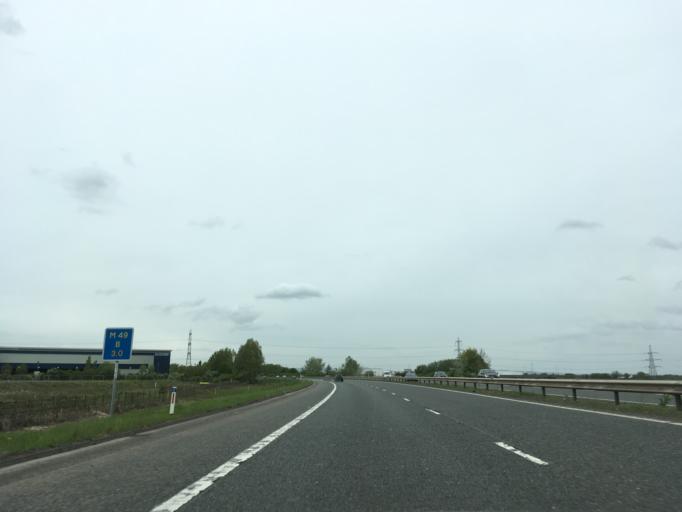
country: GB
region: England
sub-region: South Gloucestershire
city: Severn Beach
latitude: 51.5454
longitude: -2.6378
